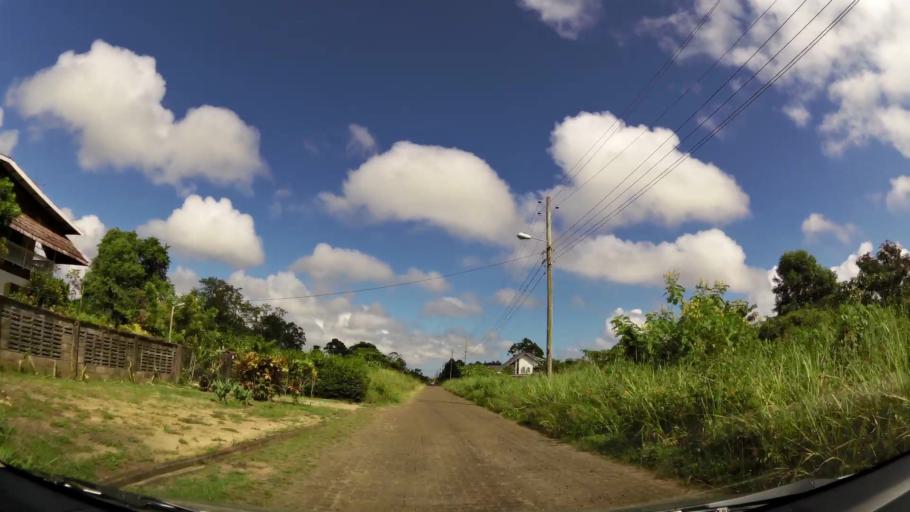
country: SR
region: Commewijne
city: Nieuw Amsterdam
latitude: 5.8751
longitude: -55.1063
